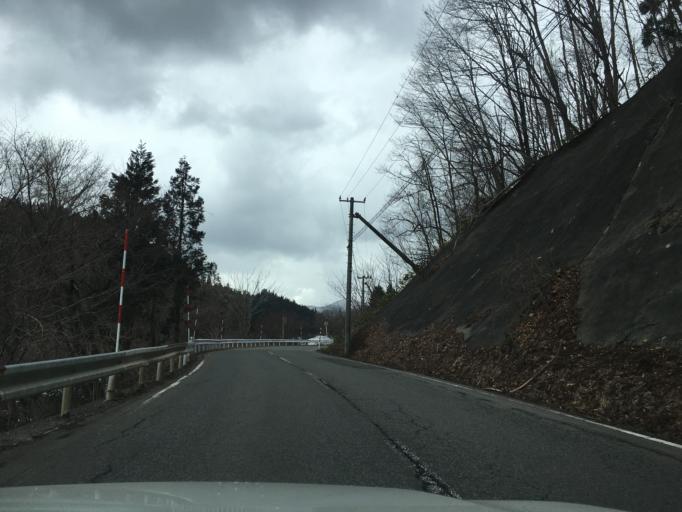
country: JP
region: Akita
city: Odate
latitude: 40.4262
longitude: 140.6544
